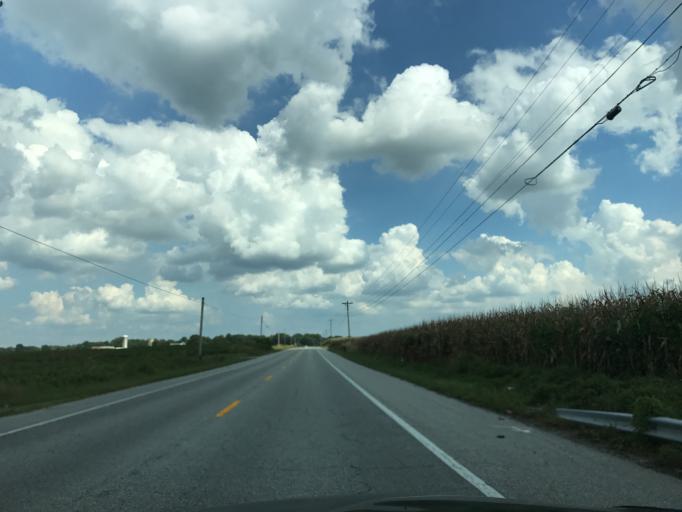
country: US
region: Maryland
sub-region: Queen Anne's County
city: Kingstown
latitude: 39.1787
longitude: -75.9065
